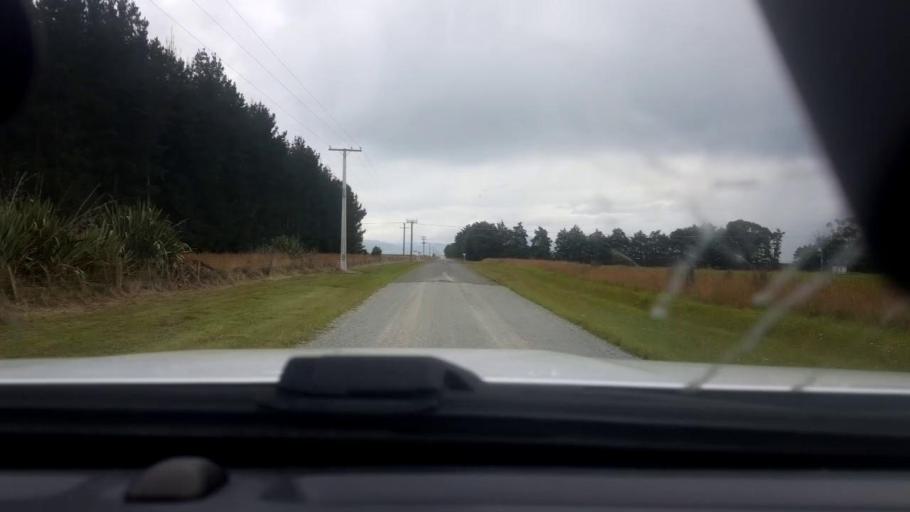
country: NZ
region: Canterbury
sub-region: Timaru District
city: Timaru
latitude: -44.1602
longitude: 171.4040
